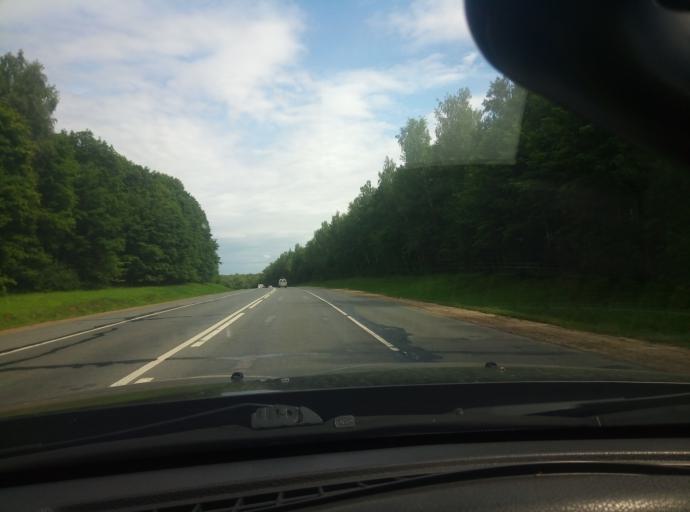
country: RU
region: Tula
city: Barsuki
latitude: 54.3215
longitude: 37.5520
